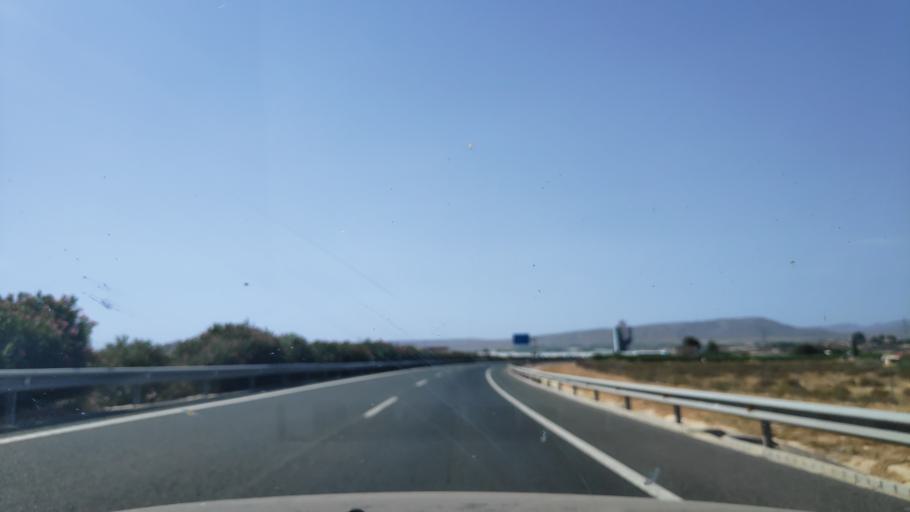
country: ES
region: Murcia
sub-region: Murcia
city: Blanca
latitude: 38.2067
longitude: -1.3490
